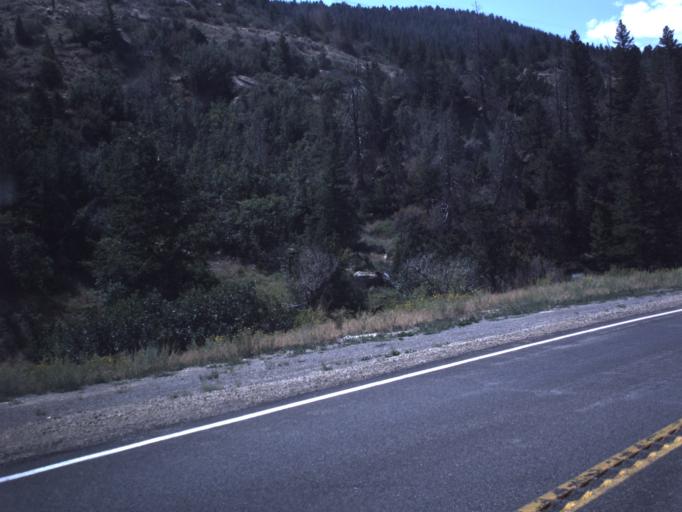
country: US
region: Utah
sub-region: Carbon County
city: Helper
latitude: 39.7617
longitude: -110.8127
